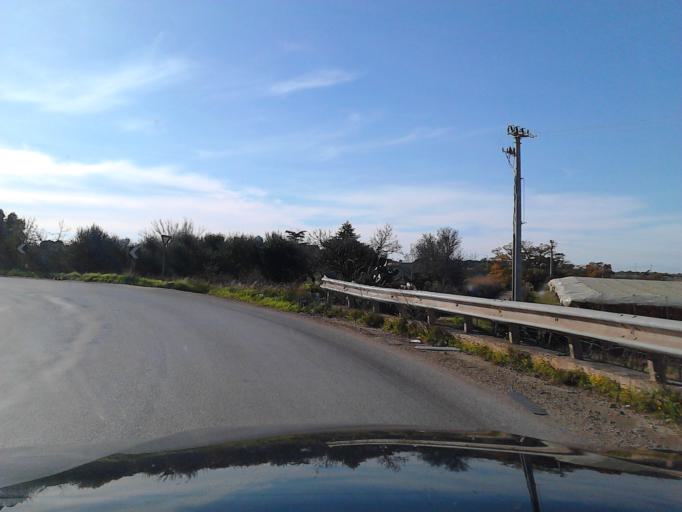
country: IT
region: Apulia
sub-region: Provincia di Bari
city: Rutigliano
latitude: 41.0090
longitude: 16.9893
